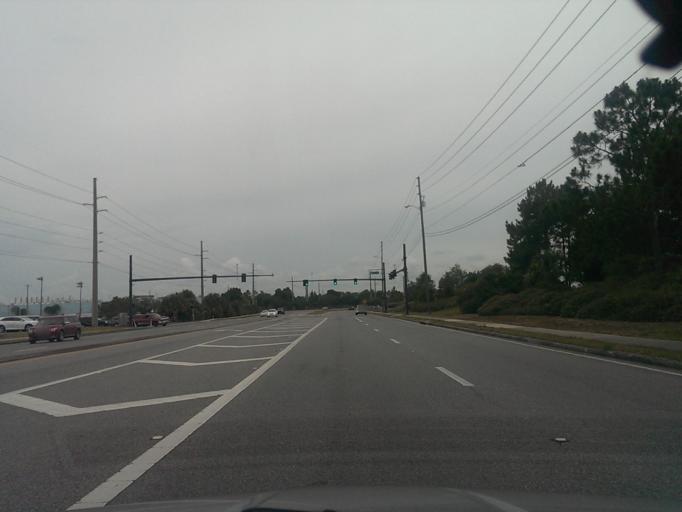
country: US
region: Florida
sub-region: Orange County
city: Doctor Phillips
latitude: 28.3986
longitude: -81.5273
